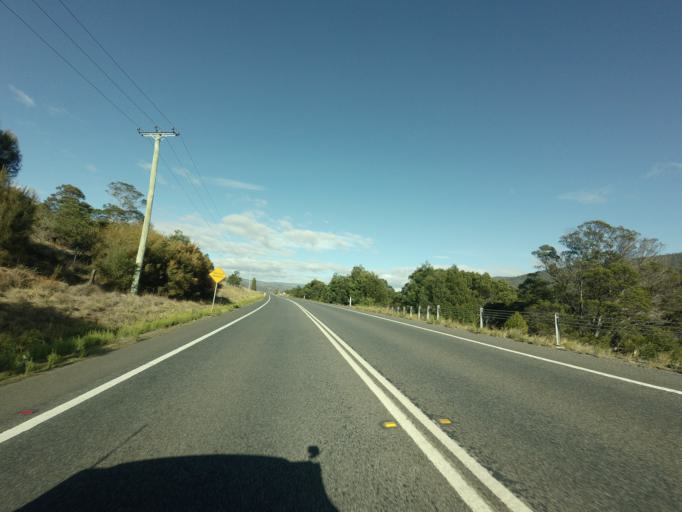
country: AU
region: Tasmania
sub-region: Glenorchy
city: Granton
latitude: -42.7585
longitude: 147.1496
